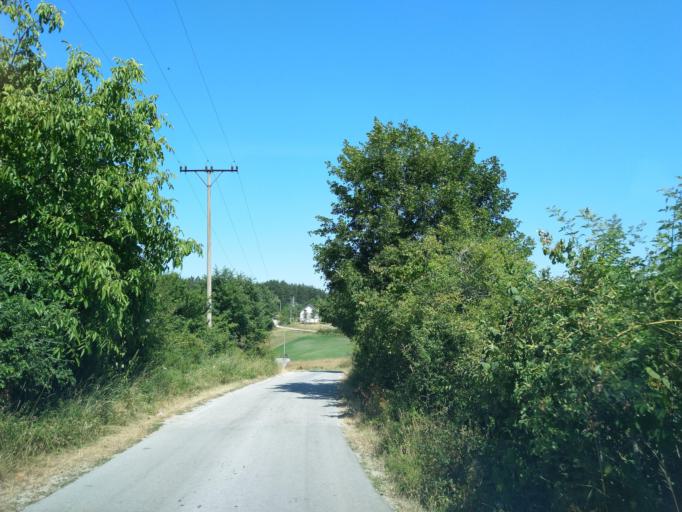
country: RS
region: Central Serbia
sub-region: Zlatiborski Okrug
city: Uzice
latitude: 43.8048
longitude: 19.8372
